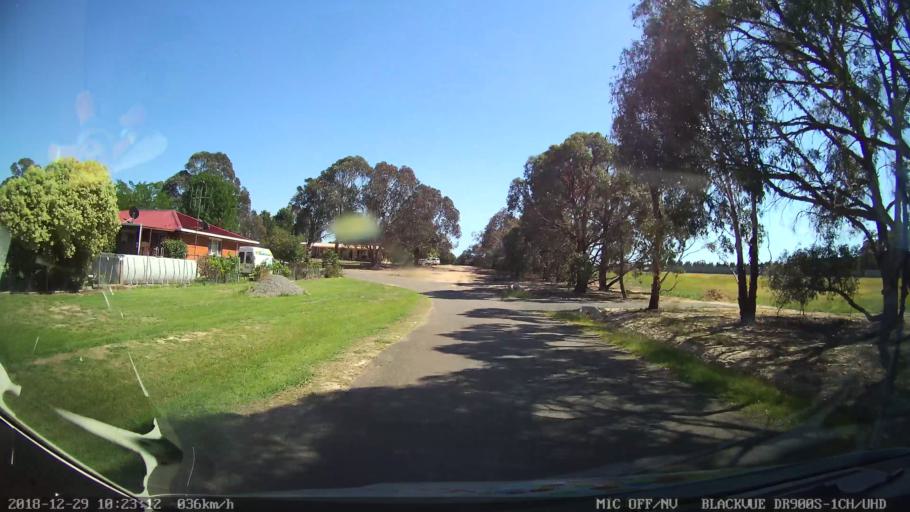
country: AU
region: New South Wales
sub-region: Yass Valley
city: Gundaroo
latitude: -34.9148
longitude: 149.4385
